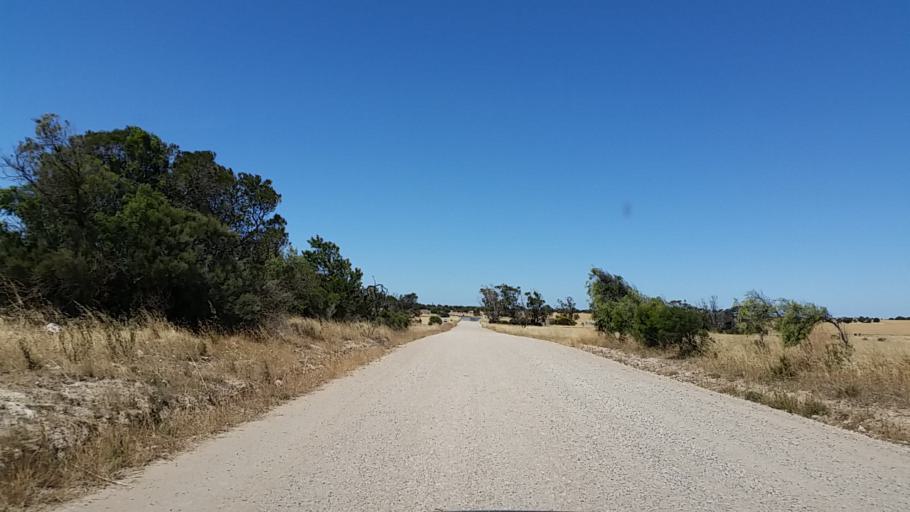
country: AU
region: South Australia
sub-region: Yorke Peninsula
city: Honiton
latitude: -35.0706
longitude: 137.5286
